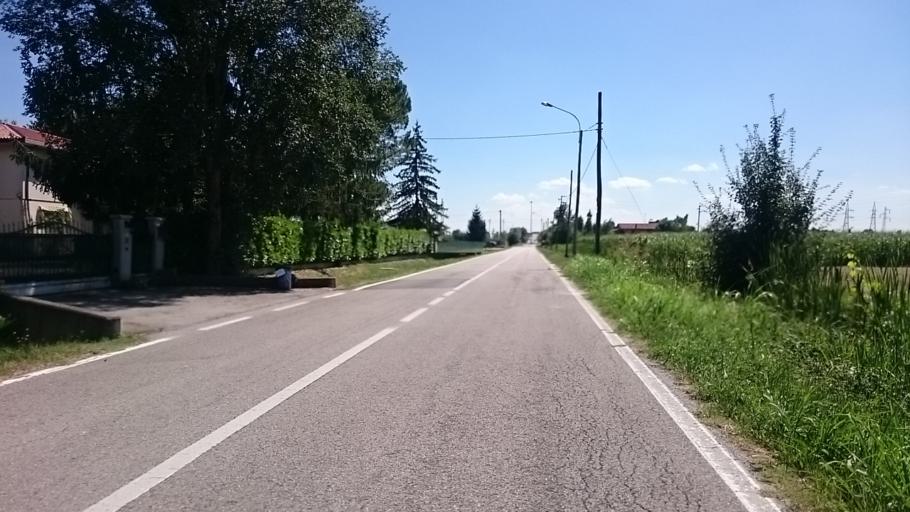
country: IT
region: Veneto
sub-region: Provincia di Venezia
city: Pianiga
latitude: 45.4508
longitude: 12.0285
